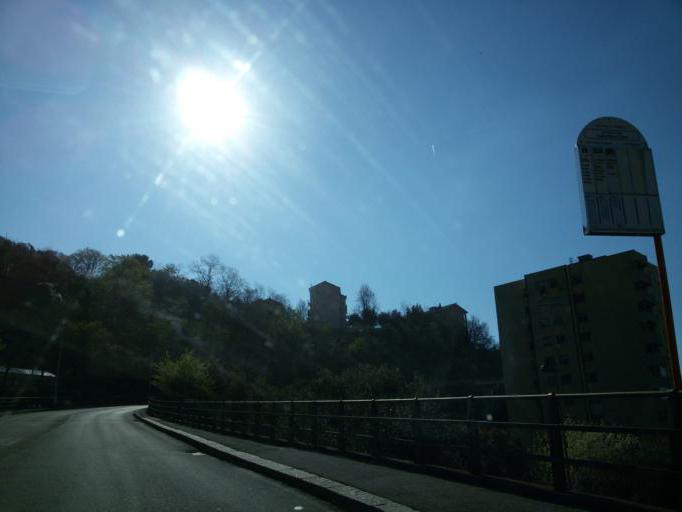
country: IT
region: Liguria
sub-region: Provincia di Genova
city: Genoa
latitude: 44.4264
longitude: 8.9087
